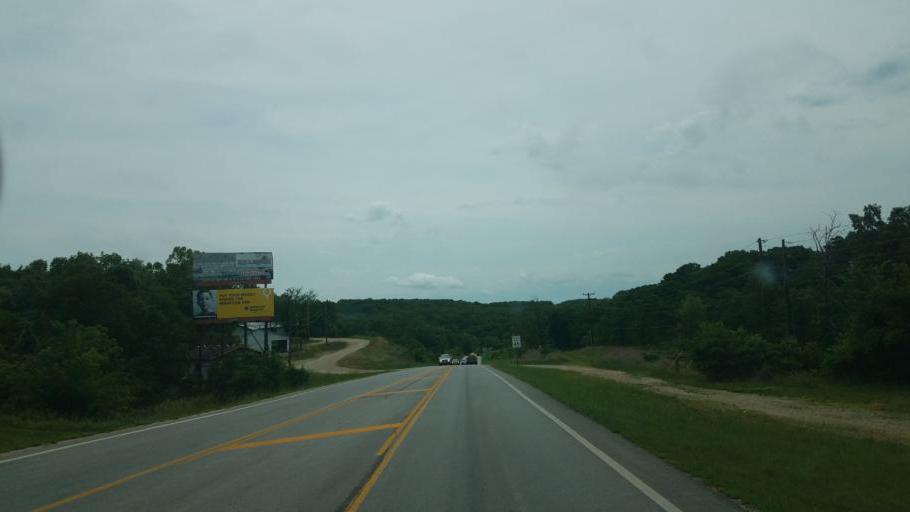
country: US
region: Missouri
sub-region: Camden County
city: Four Seasons
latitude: 38.1745
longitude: -92.7825
